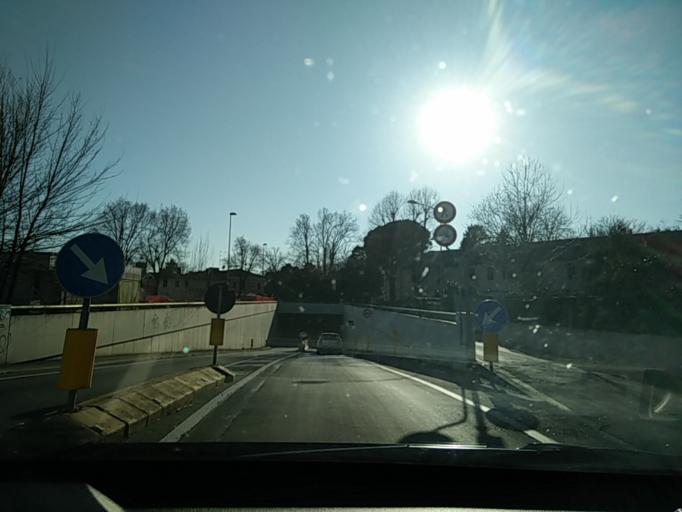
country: IT
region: Veneto
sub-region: Provincia di Treviso
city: Oderzo
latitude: 45.7762
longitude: 12.4908
